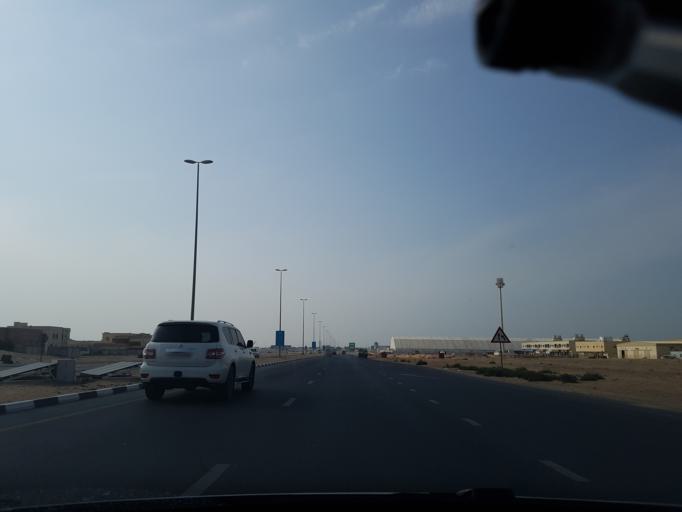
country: AE
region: Ajman
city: Ajman
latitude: 25.4312
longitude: 55.5117
